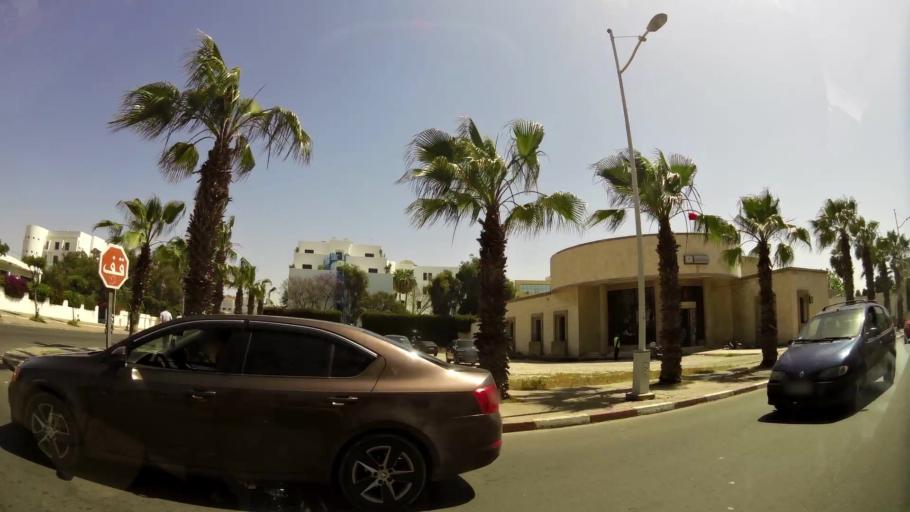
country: MA
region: Souss-Massa-Draa
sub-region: Agadir-Ida-ou-Tnan
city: Agadir
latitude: 30.4113
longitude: -9.5835
